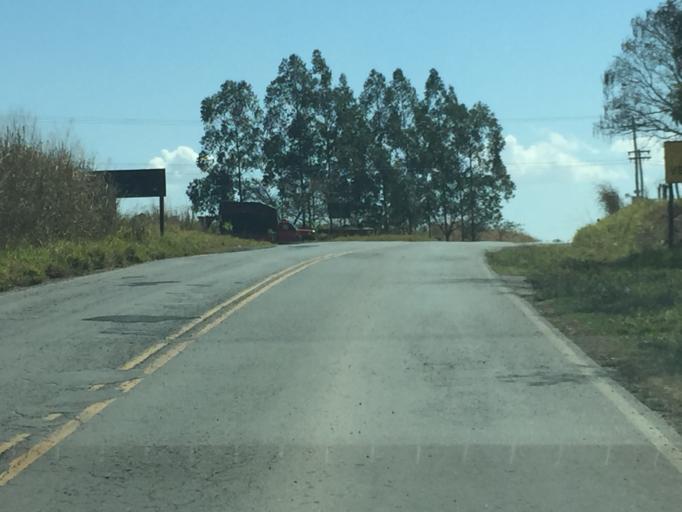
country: BR
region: Sao Paulo
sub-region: Moji-Guacu
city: Mogi-Gaucu
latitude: -22.3376
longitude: -46.8826
